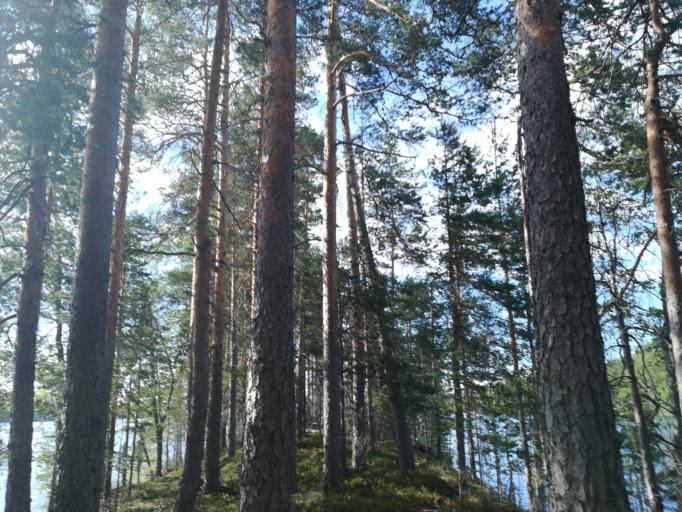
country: FI
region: Southern Savonia
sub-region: Savonlinna
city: Savonlinna
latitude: 61.6446
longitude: 28.7084
